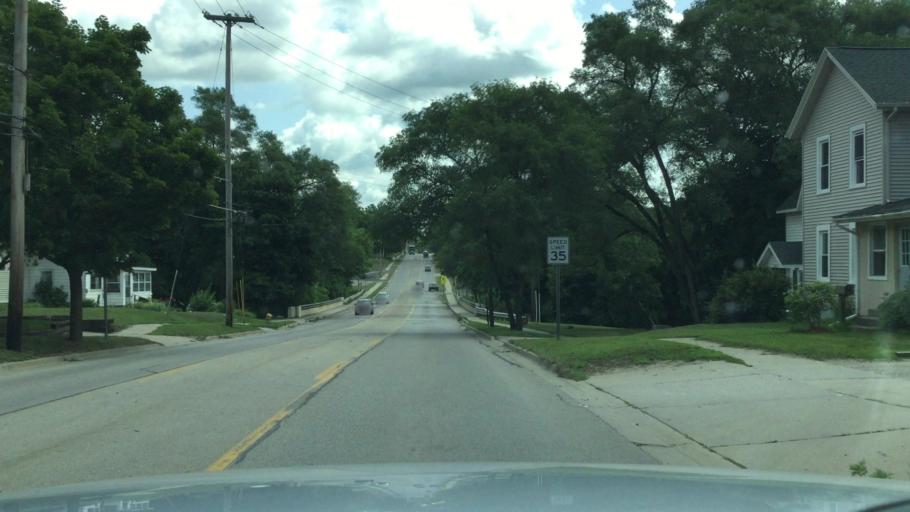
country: US
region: Michigan
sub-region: Montcalm County
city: Greenville
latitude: 43.1774
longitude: -85.2492
